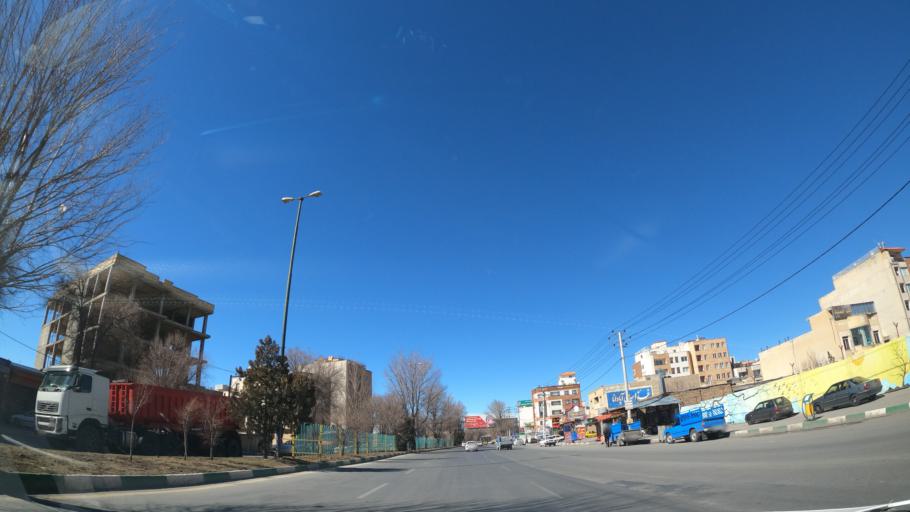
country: IR
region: Chahar Mahall va Bakhtiari
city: Shahrekord
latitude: 32.3105
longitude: 50.8896
